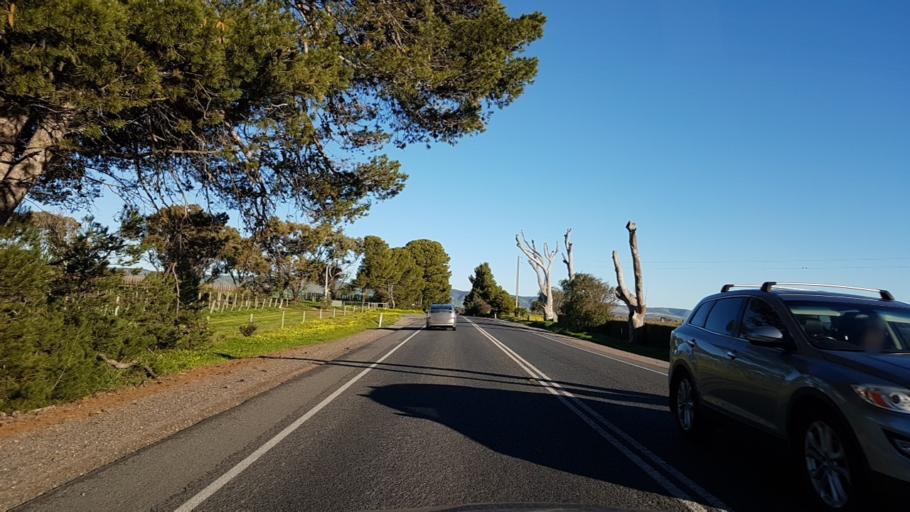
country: AU
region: South Australia
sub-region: Onkaparinga
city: Moana
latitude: -35.2370
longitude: 138.4936
